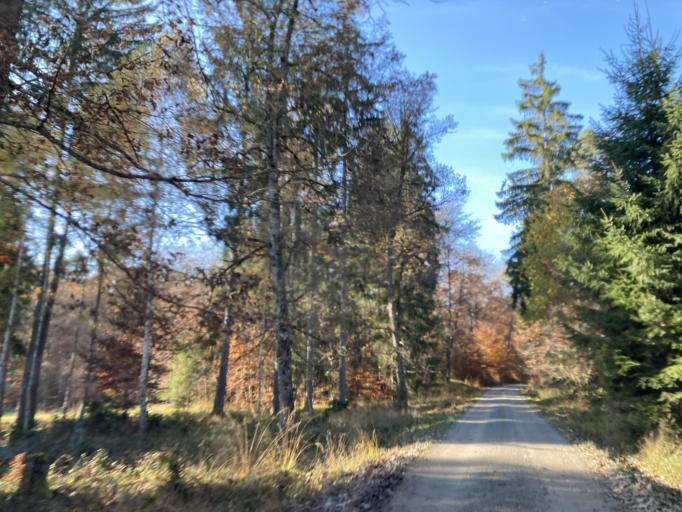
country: DE
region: Baden-Wuerttemberg
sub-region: Regierungsbezirk Stuttgart
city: Altdorf
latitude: 48.5700
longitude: 9.0103
